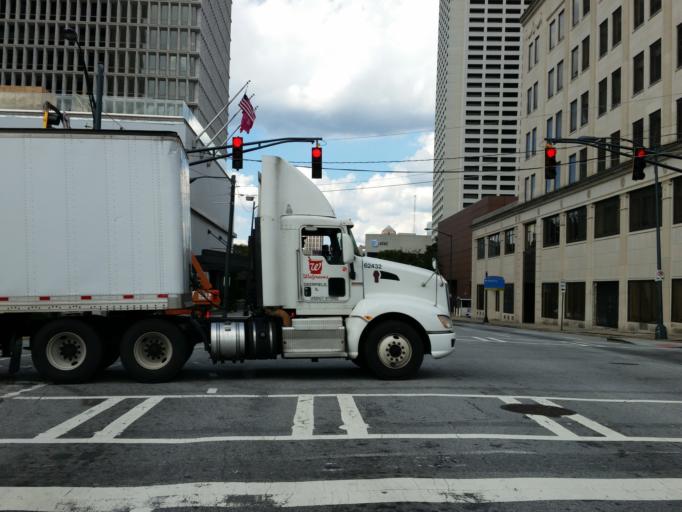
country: US
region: Georgia
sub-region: Fulton County
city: Atlanta
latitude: 33.7697
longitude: -84.3875
